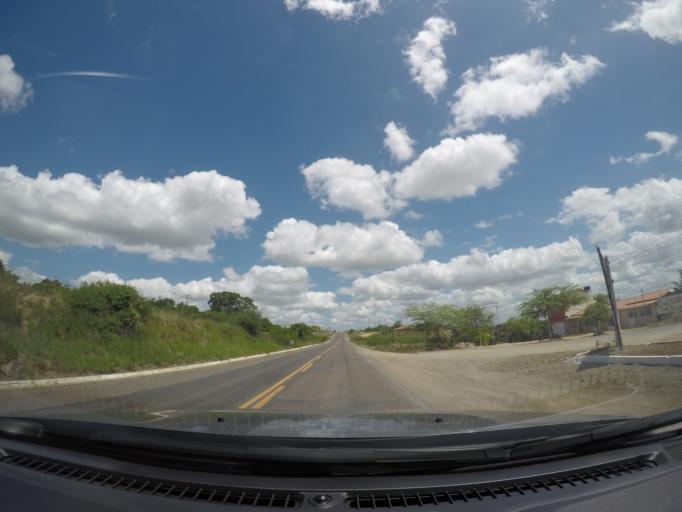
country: BR
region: Bahia
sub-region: Ipira
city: Ipira
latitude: -12.1849
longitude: -39.7077
